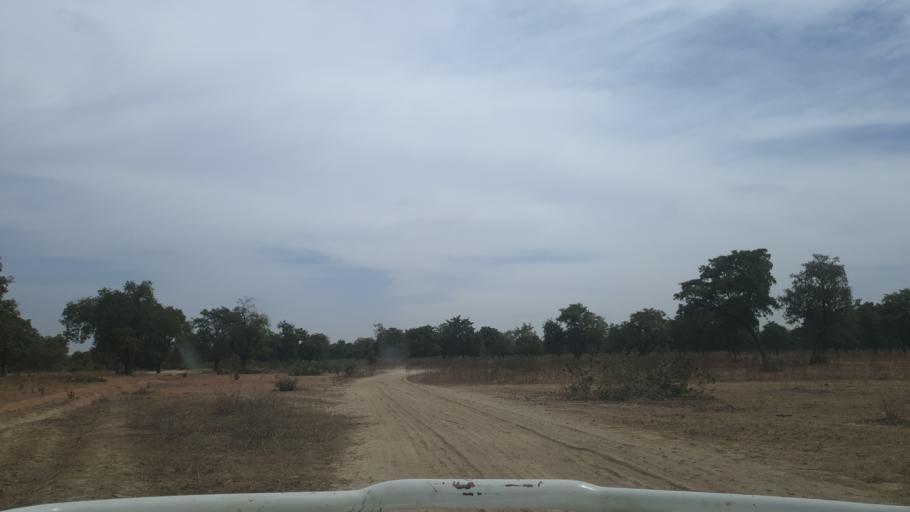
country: ML
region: Sikasso
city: Yorosso
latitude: 12.2400
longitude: -4.7352
